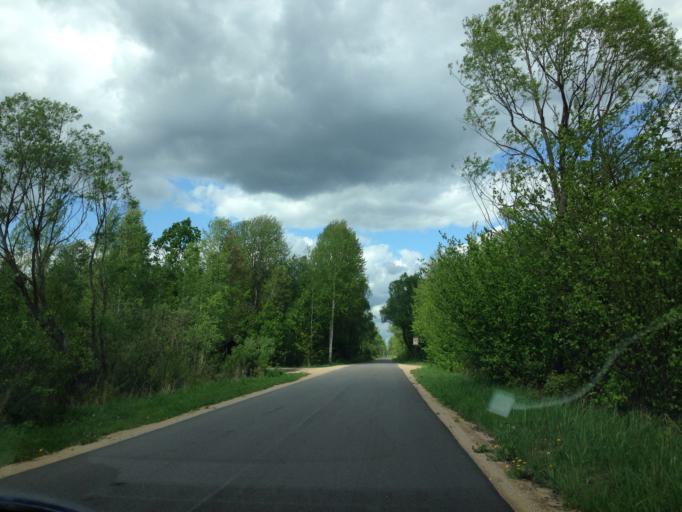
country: PL
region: Podlasie
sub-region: Powiat bialostocki
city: Tykocin
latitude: 53.2992
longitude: 22.6049
